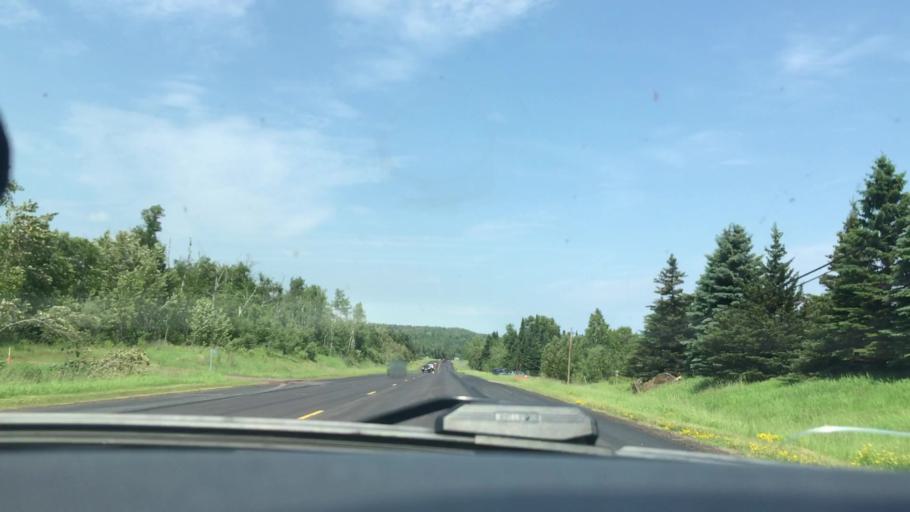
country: US
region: Minnesota
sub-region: Lake County
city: Silver Bay
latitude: 47.3284
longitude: -91.2099
